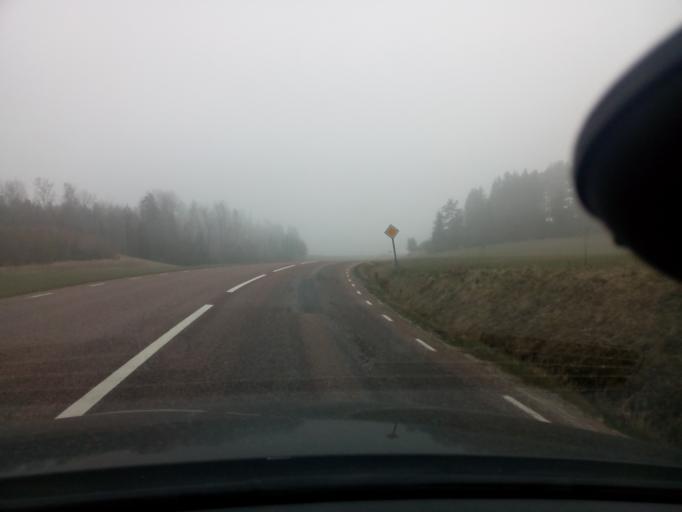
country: SE
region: Soedermanland
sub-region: Nykopings Kommun
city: Nykoping
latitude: 58.8623
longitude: 17.0652
